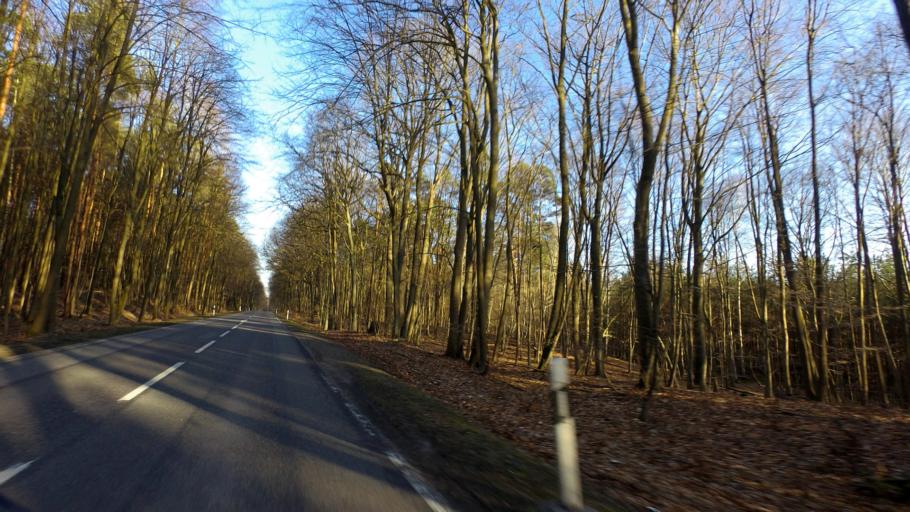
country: DE
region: Brandenburg
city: Joachimsthal
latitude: 52.9554
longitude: 13.7589
